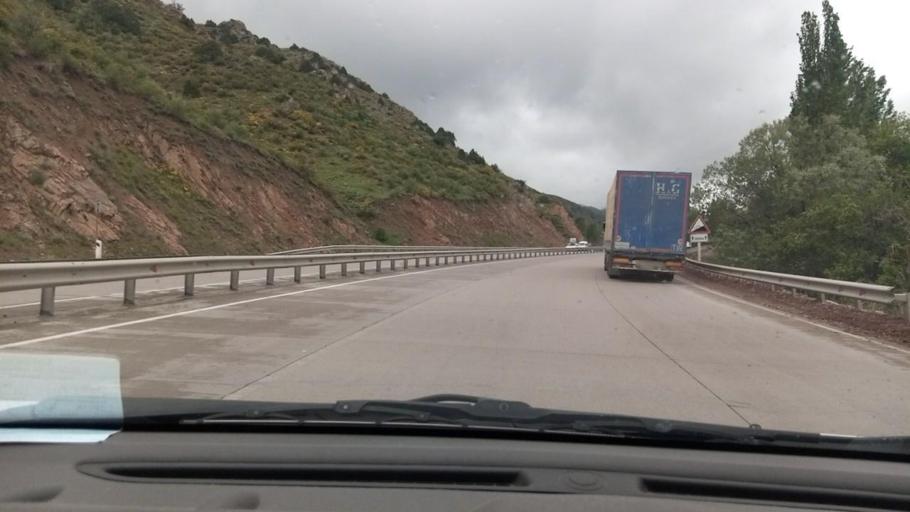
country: TJ
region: Viloyati Sughd
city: Shaydon
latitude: 41.0354
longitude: 70.5827
